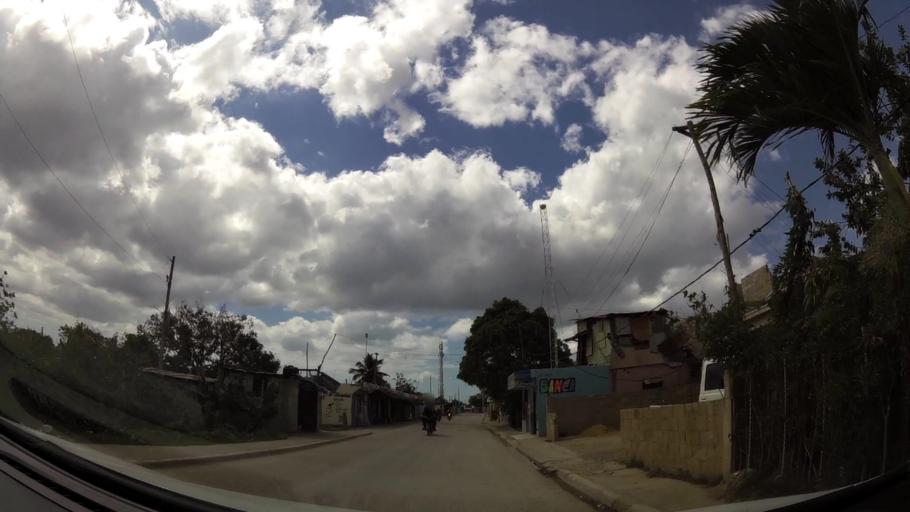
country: DO
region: Santo Domingo
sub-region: Santo Domingo
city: Boca Chica
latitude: 18.4510
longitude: -69.6353
